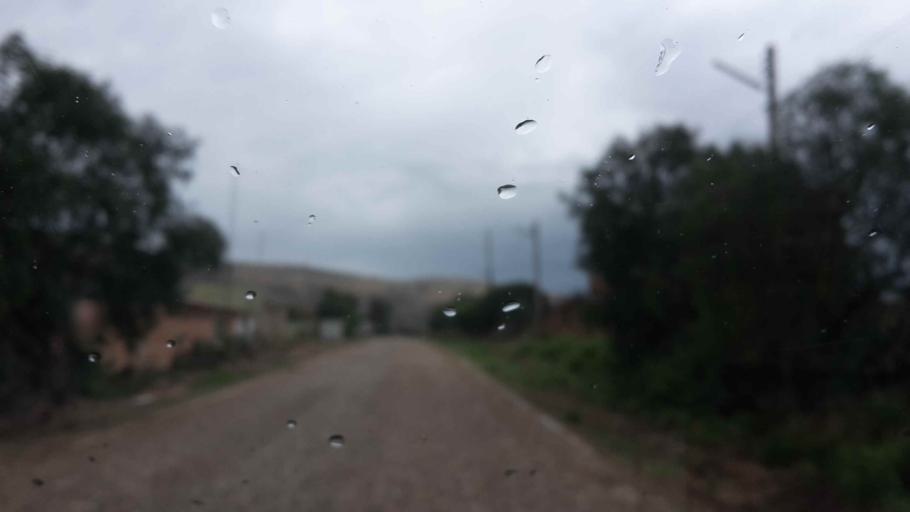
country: BO
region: Cochabamba
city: Tarata
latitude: -17.5494
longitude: -66.1658
